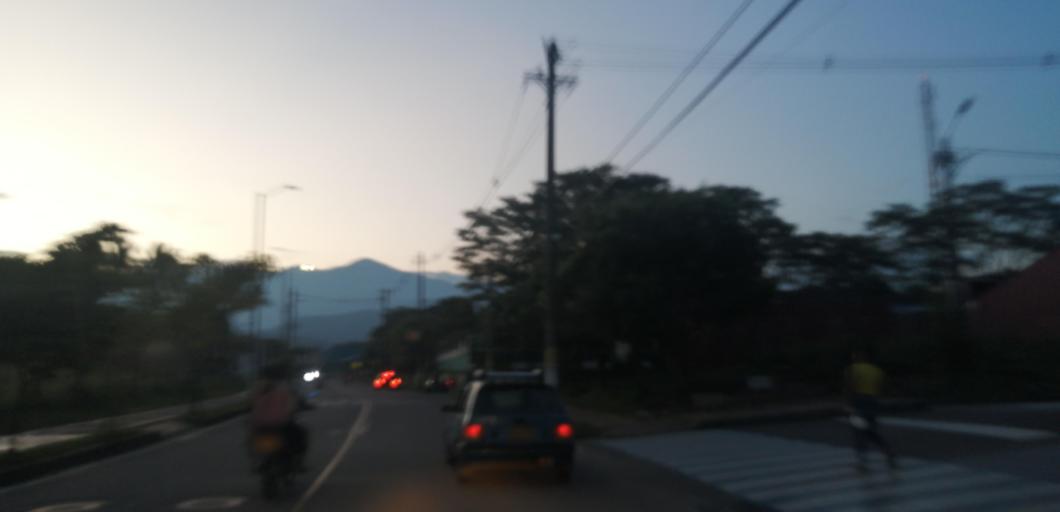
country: CO
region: Meta
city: Acacias
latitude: 3.9907
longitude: -73.7809
